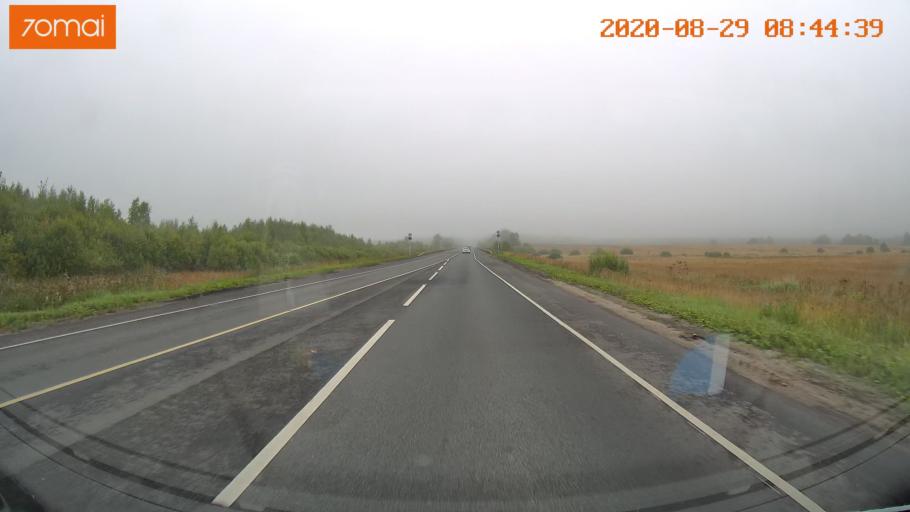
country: RU
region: Ivanovo
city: Rodniki
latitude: 57.1206
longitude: 41.7913
